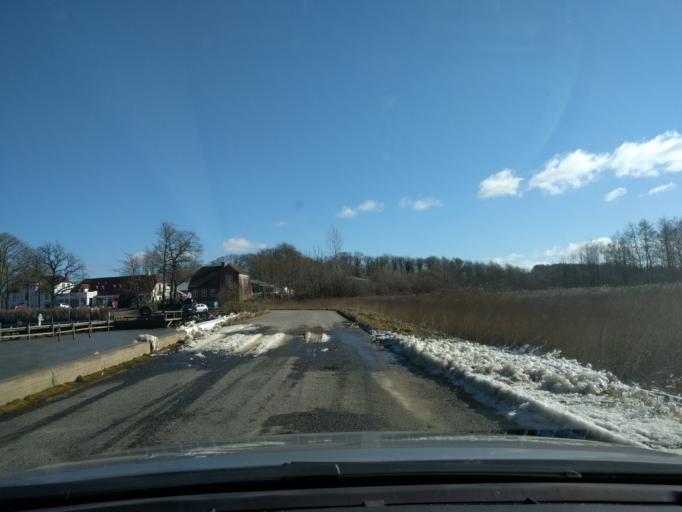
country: DK
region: South Denmark
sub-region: Aabenraa Kommune
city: Lojt Kirkeby
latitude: 55.1220
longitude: 9.4647
